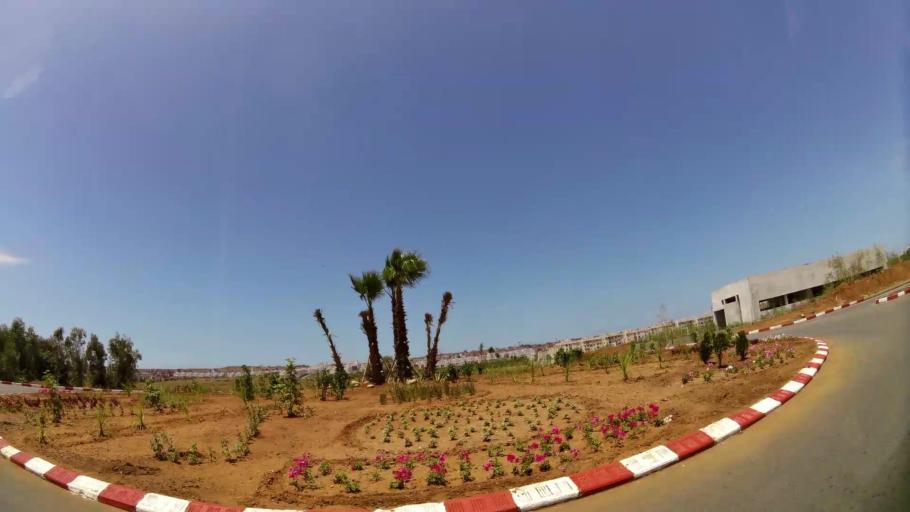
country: MA
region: Gharb-Chrarda-Beni Hssen
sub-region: Kenitra Province
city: Kenitra
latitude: 34.2464
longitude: -6.6388
